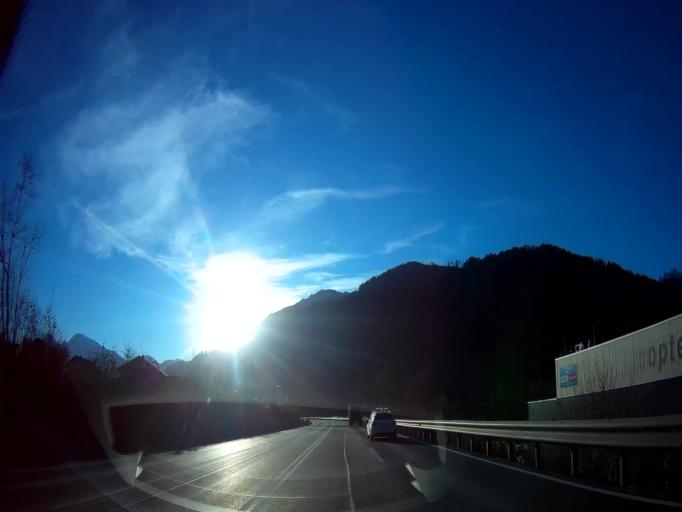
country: AT
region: Salzburg
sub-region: Politischer Bezirk Sankt Johann im Pongau
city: Bischofshofen
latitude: 47.3934
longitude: 13.2258
